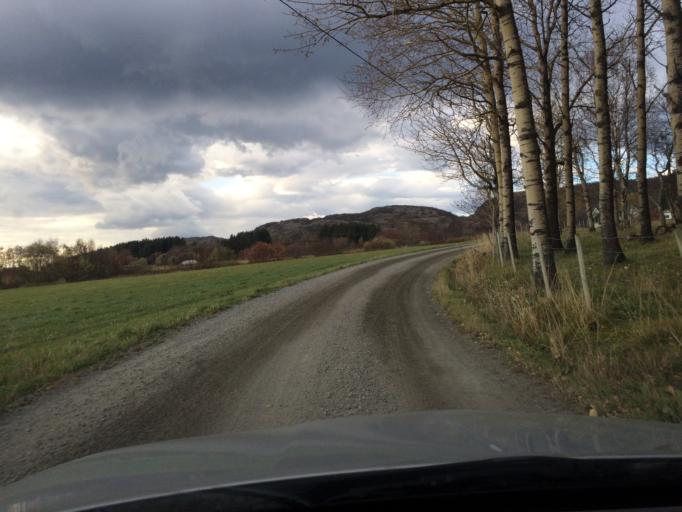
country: NO
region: Nordland
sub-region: Vevelstad
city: Vevelstad
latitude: 65.7725
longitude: 12.4550
